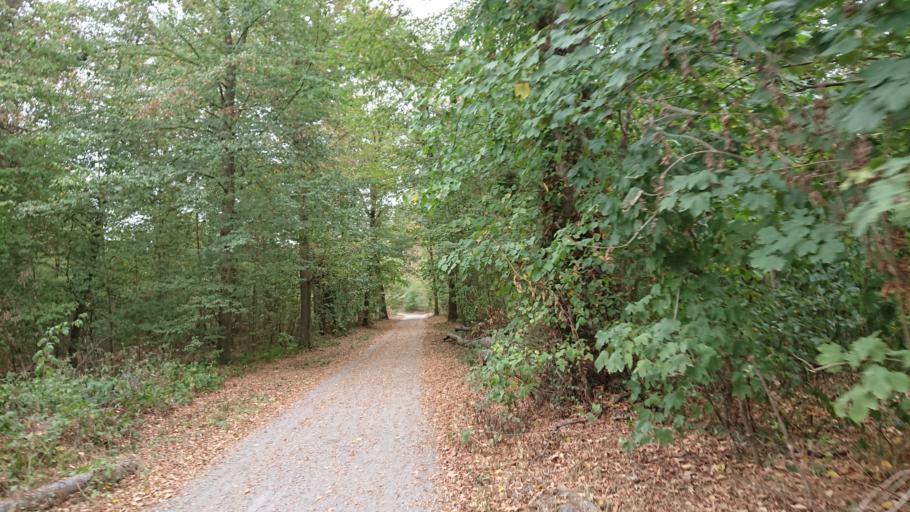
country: DE
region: Baden-Wuerttemberg
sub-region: Karlsruhe Region
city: Karlsruhe
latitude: 48.9863
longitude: 8.4129
